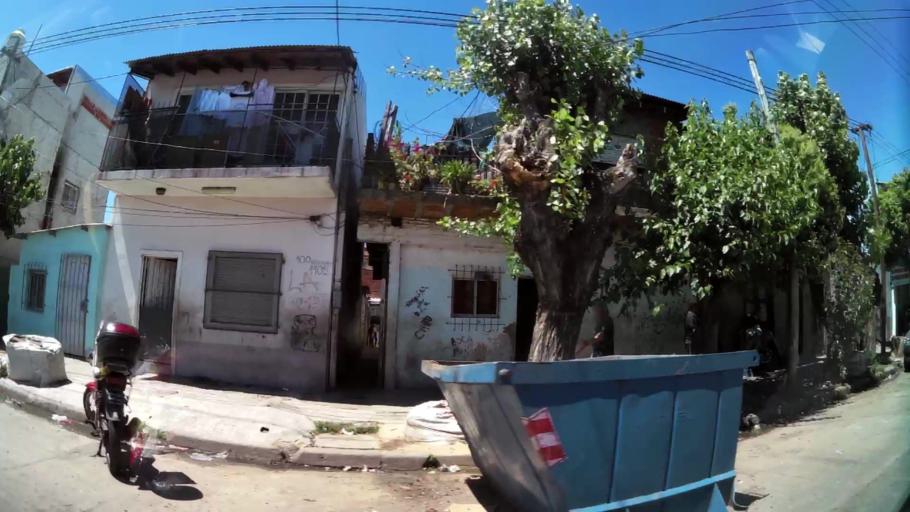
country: AR
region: Buenos Aires
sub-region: Partido de San Isidro
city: San Isidro
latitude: -34.4619
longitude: -58.5466
